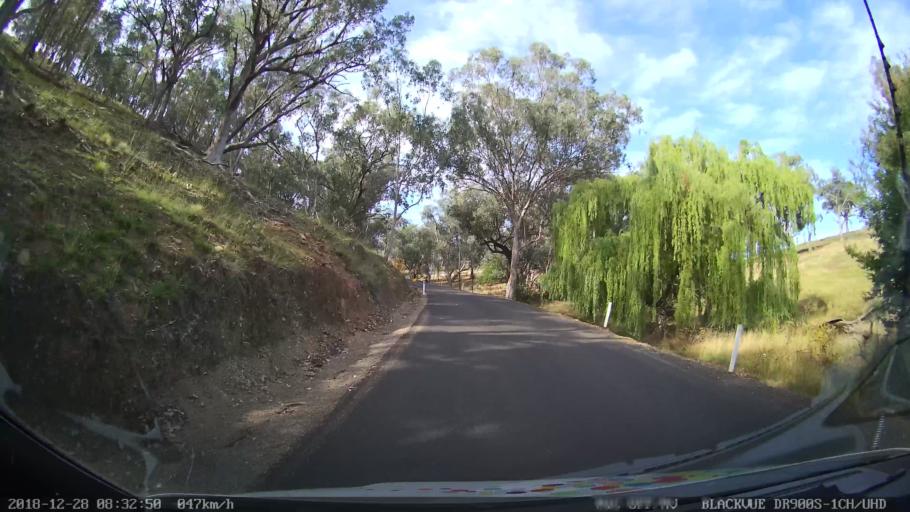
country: AU
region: New South Wales
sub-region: Blayney
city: Blayney
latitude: -33.9641
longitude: 149.3110
